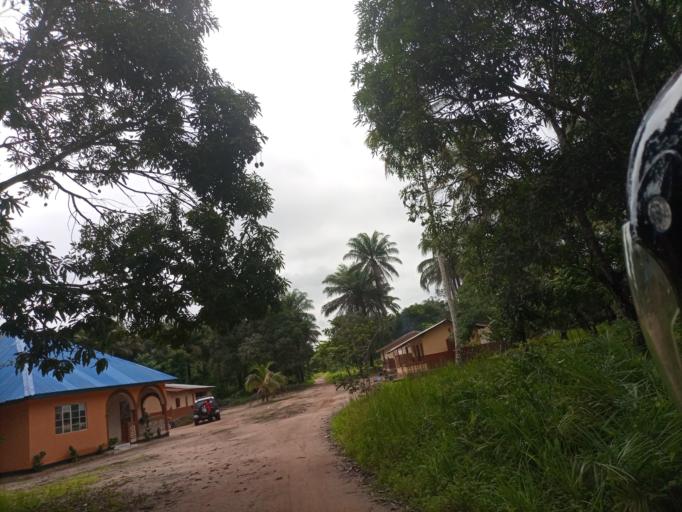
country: SL
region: Northern Province
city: Sawkta
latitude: 8.6548
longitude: -13.1758
